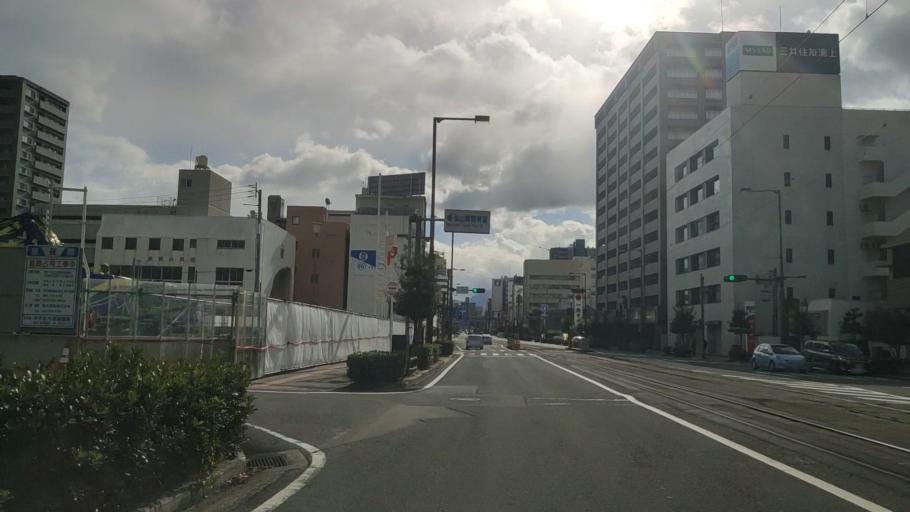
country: JP
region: Ehime
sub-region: Shikoku-chuo Shi
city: Matsuyama
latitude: 33.8449
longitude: 132.7755
